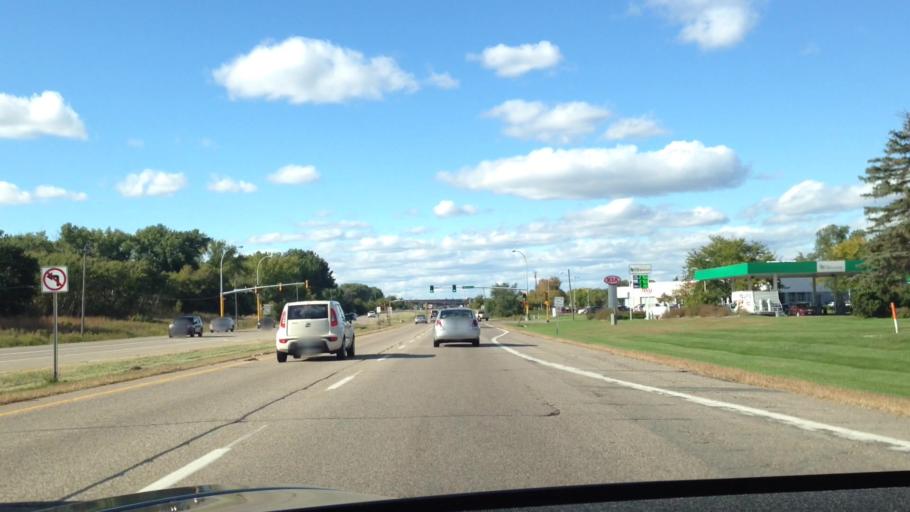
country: US
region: Minnesota
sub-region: Hennepin County
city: Osseo
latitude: 45.0973
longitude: -93.3852
